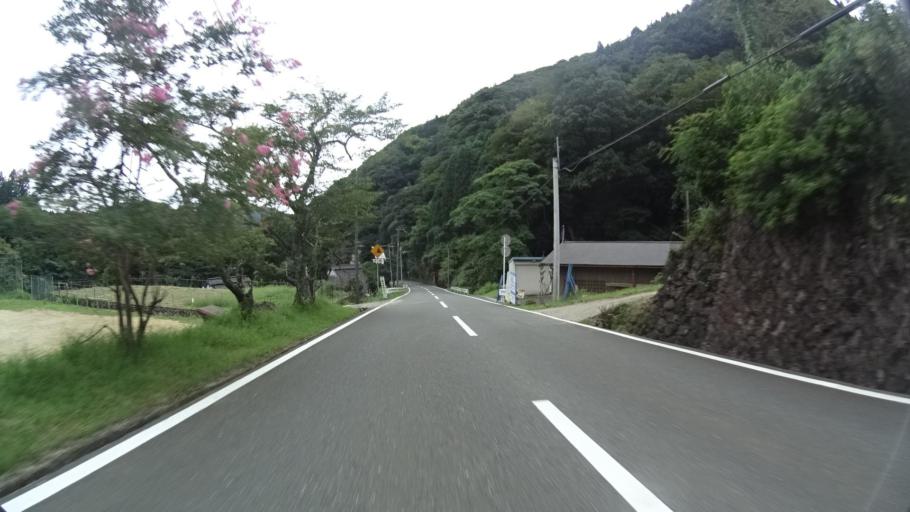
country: JP
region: Kyoto
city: Miyazu
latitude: 35.4451
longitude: 135.1488
